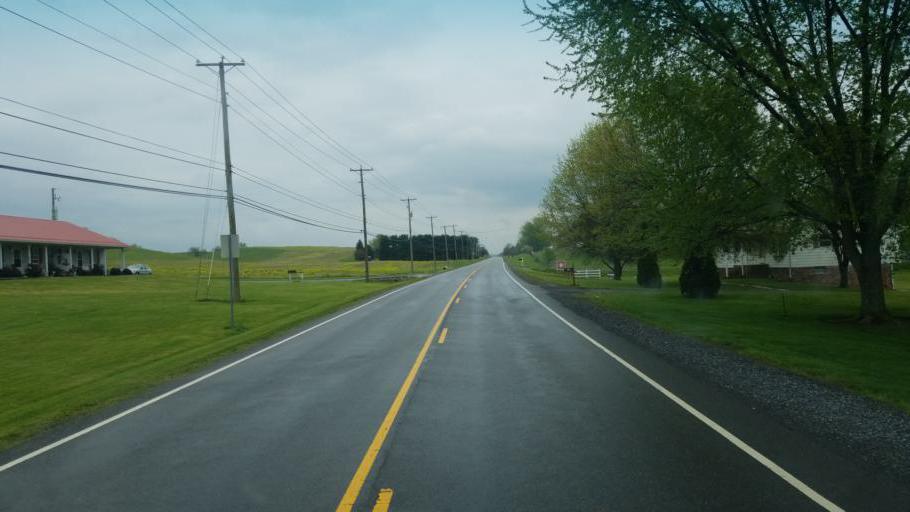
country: US
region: Virginia
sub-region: Smyth County
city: Atkins
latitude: 36.8876
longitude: -81.3669
